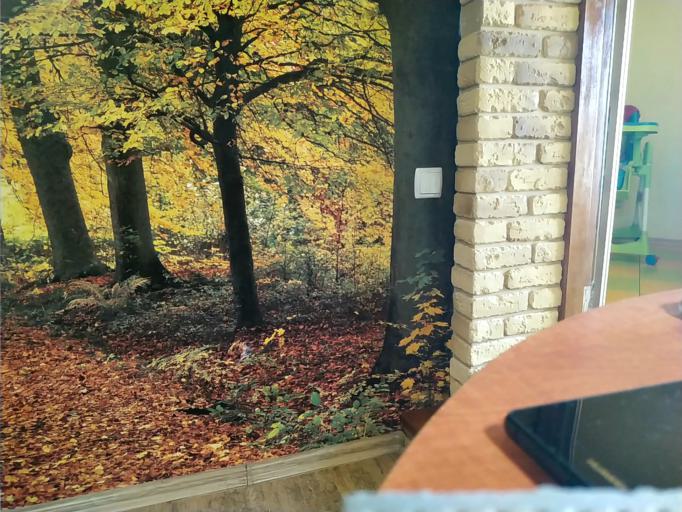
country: RU
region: Kaluga
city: Kondrovo
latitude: 54.8016
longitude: 35.9247
